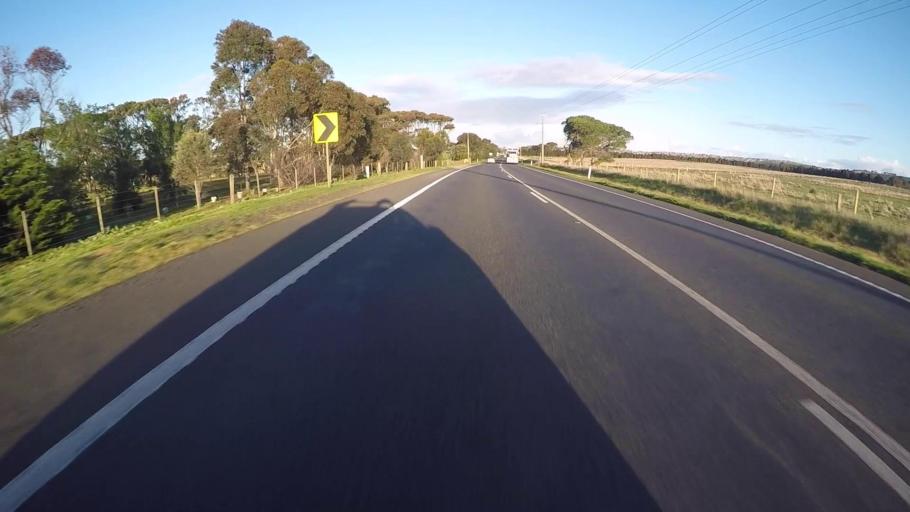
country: AU
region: Victoria
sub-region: Greater Geelong
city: Wandana Heights
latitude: -38.1354
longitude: 144.2817
